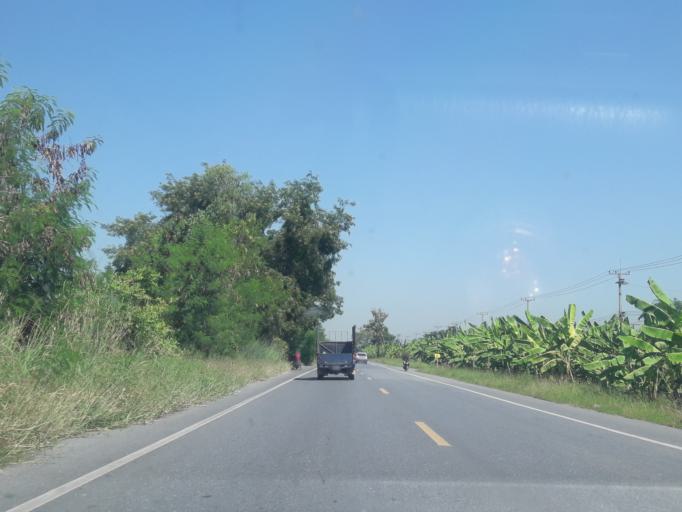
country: TH
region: Sara Buri
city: Nong Khae
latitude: 14.2569
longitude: 100.8234
